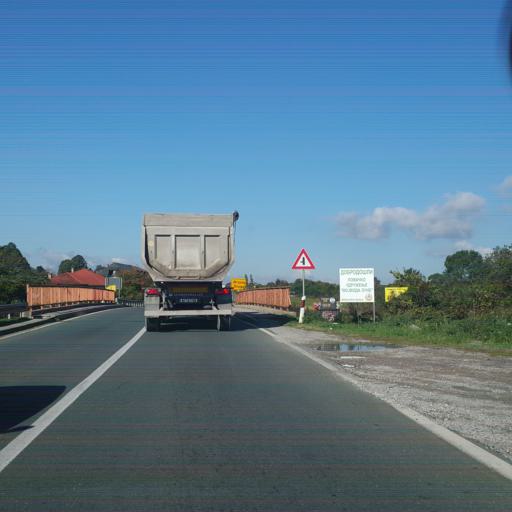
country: RS
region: Central Serbia
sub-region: Rasinski Okrug
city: Trstenik
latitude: 43.6313
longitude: 20.9657
